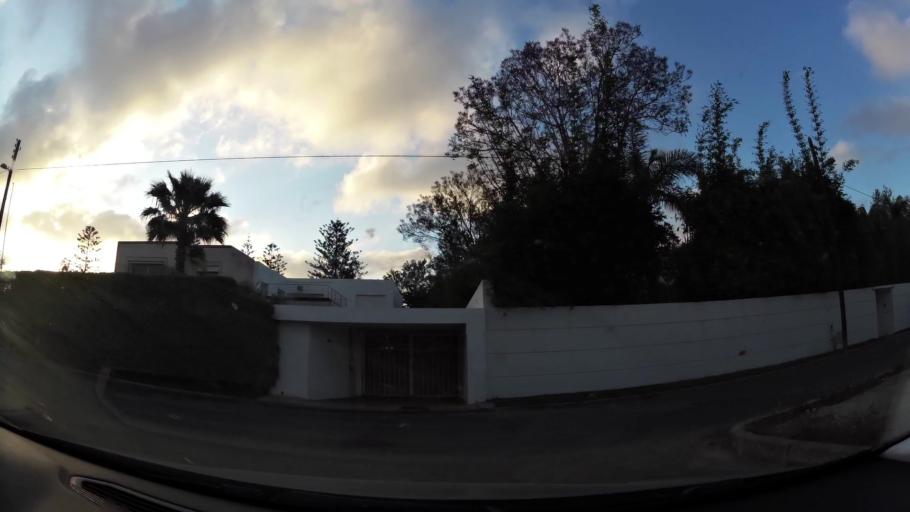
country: MA
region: Rabat-Sale-Zemmour-Zaer
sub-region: Rabat
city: Rabat
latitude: 33.9714
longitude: -6.8373
